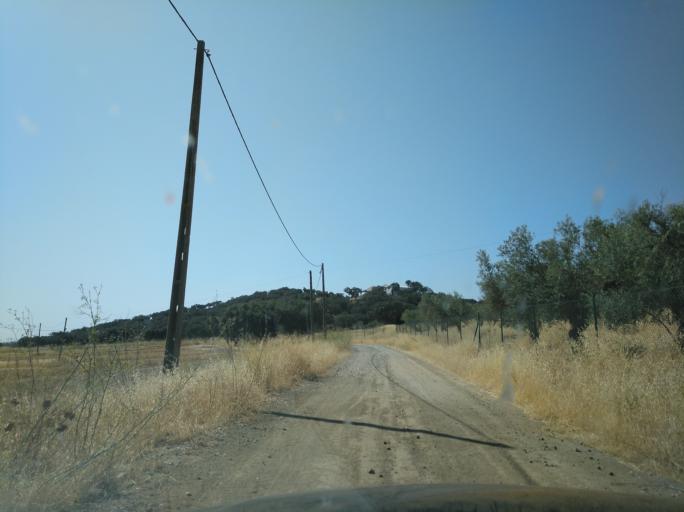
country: PT
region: Portalegre
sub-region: Campo Maior
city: Campo Maior
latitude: 39.0510
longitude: -6.9992
